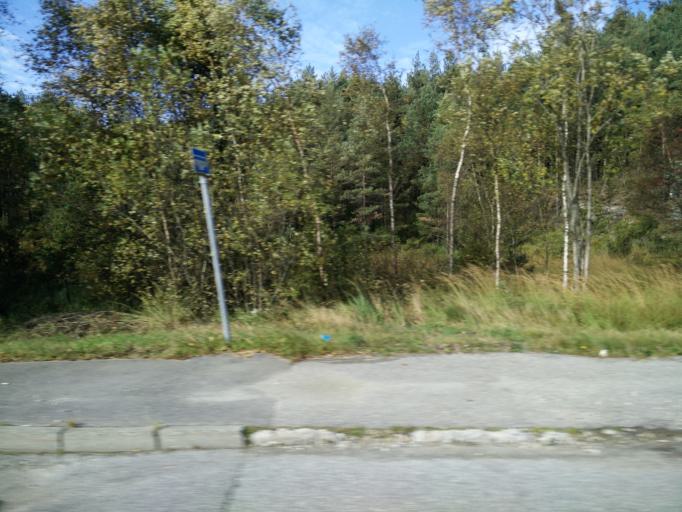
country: NO
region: Hordaland
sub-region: Sveio
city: Sveio
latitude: 59.5161
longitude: 5.3276
